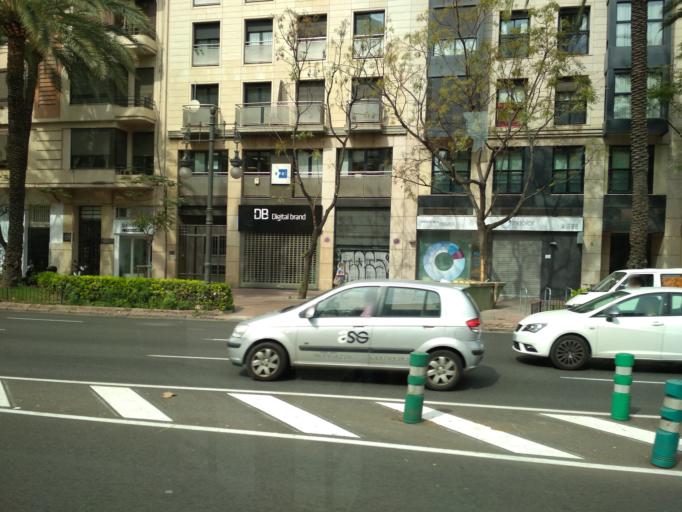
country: ES
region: Valencia
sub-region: Provincia de Valencia
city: Valencia
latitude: 39.4647
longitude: -0.3745
